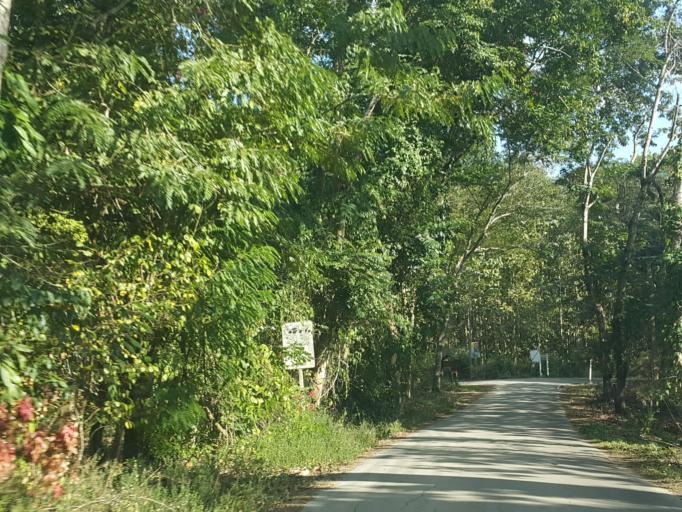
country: TH
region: Chiang Mai
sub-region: Amphoe Chiang Dao
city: Chiang Dao
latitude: 19.4000
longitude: 98.9271
